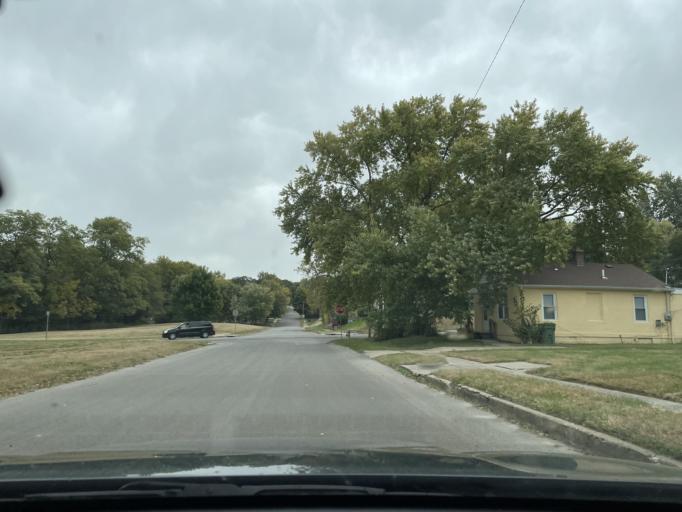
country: US
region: Missouri
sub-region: Buchanan County
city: Saint Joseph
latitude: 39.7788
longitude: -94.8397
